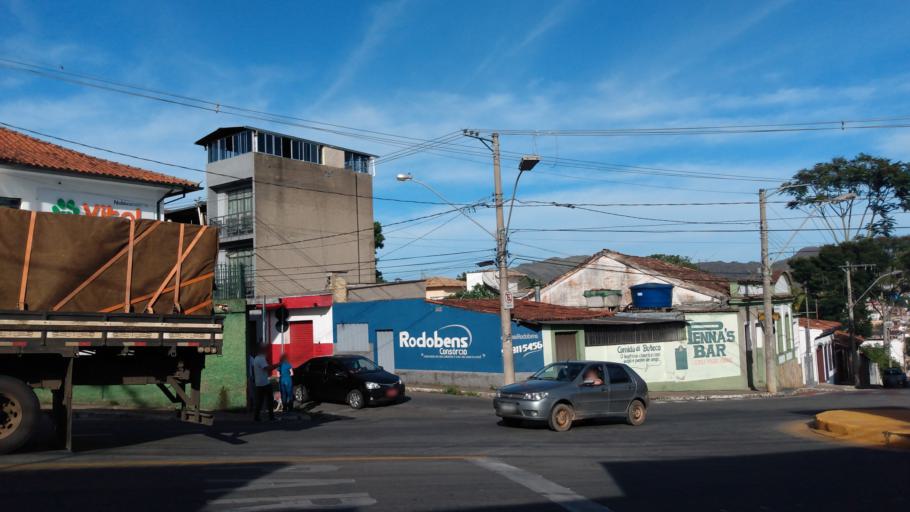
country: BR
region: Minas Gerais
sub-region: Sao Joao Del Rei
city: Sao Joao del Rei
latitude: -21.1414
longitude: -44.2574
